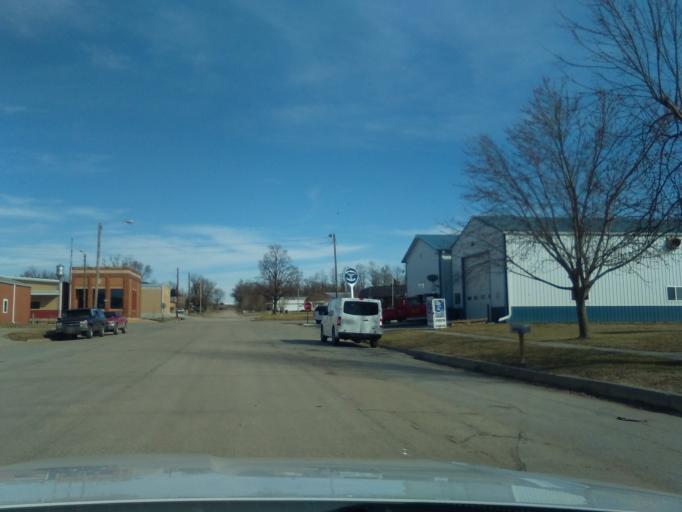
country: US
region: Nebraska
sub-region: Saline County
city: Friend
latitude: 40.7778
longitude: -97.2800
